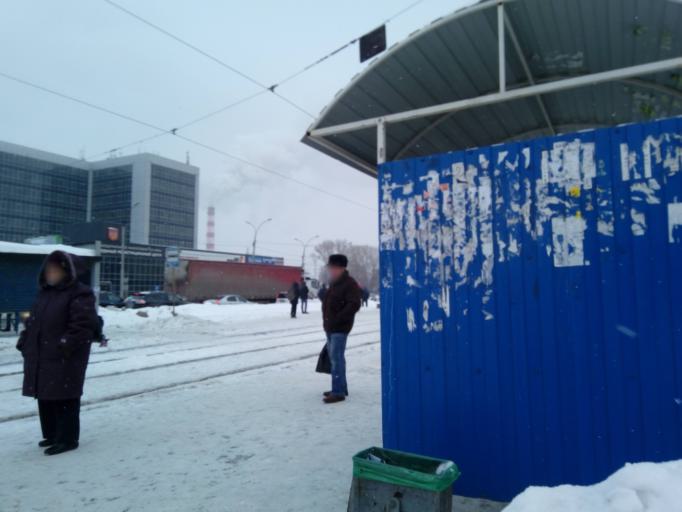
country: RU
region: Novosibirsk
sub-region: Novosibirskiy Rayon
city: Novosibirsk
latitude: 54.9945
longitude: 82.8671
